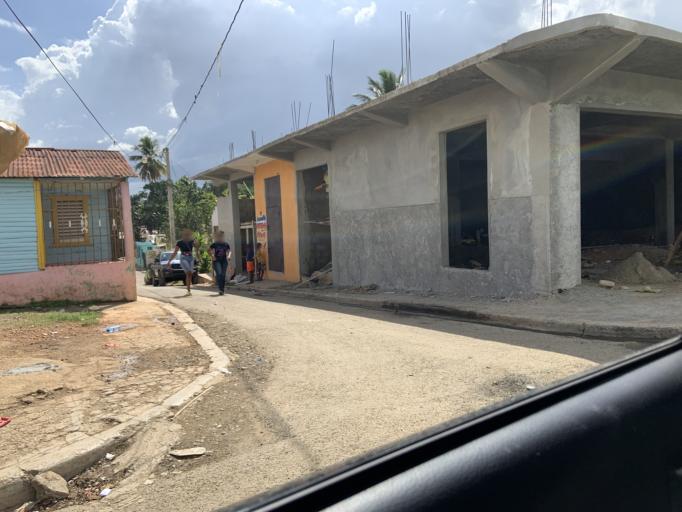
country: DO
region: Monte Plata
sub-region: Yamasa
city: Yamasa
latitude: 18.7733
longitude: -70.0295
